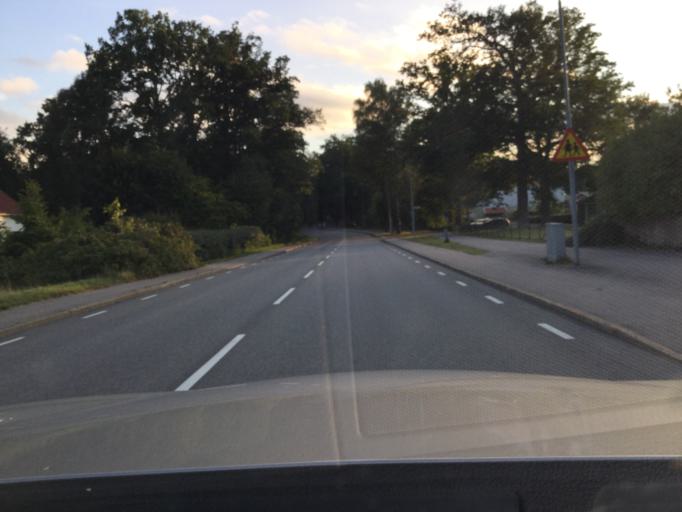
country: SE
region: Kronoberg
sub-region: Almhults Kommun
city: AElmhult
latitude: 56.6443
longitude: 14.2248
